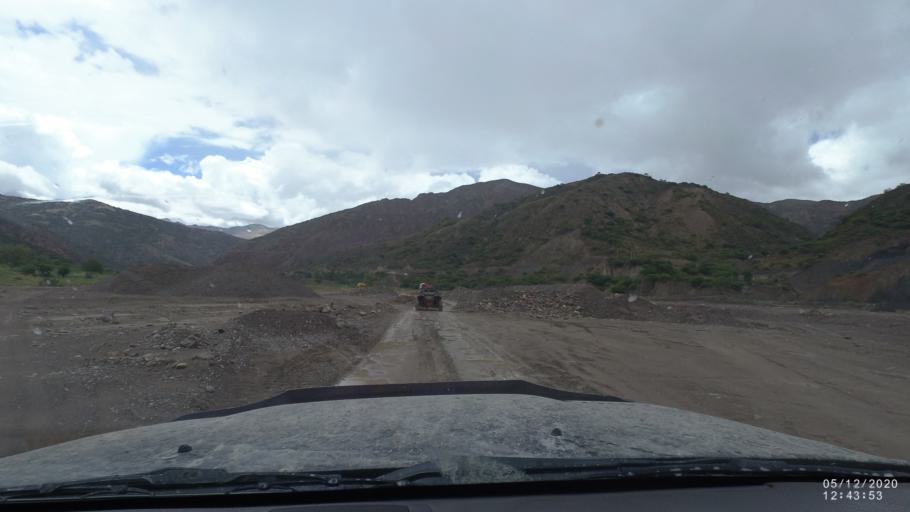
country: BO
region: Cochabamba
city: Sipe Sipe
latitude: -17.5498
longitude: -66.4379
